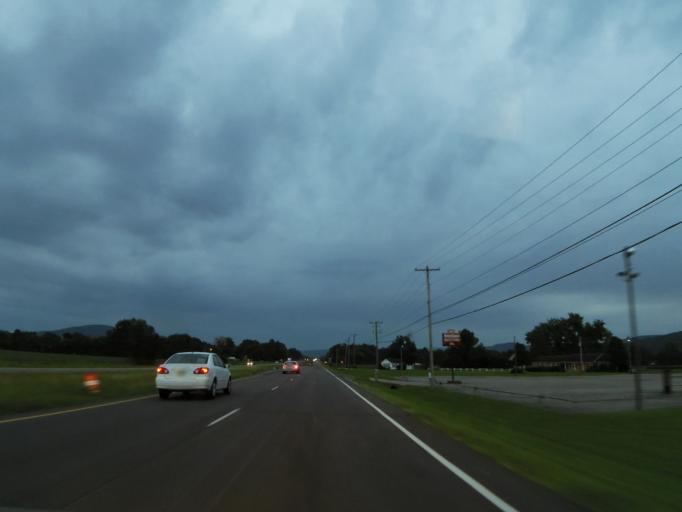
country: US
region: Alabama
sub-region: Madison County
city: Moores Mill
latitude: 34.7564
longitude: -86.4705
